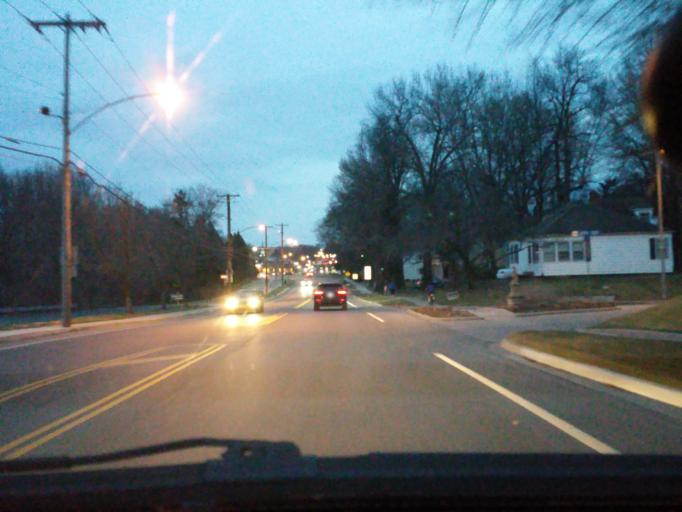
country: US
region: Kansas
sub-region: Johnson County
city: Fairway
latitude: 39.0072
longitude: -94.6304
